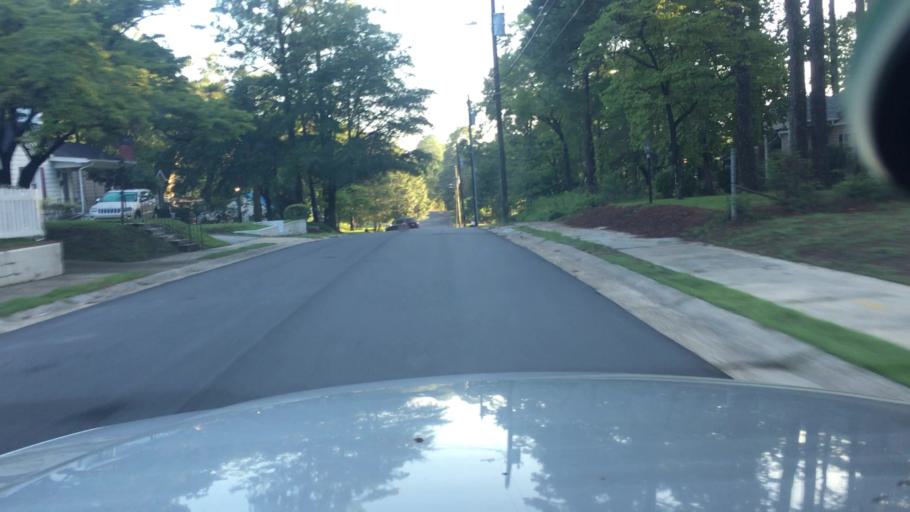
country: US
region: North Carolina
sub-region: Cumberland County
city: Fayetteville
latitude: 35.0640
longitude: -78.9073
